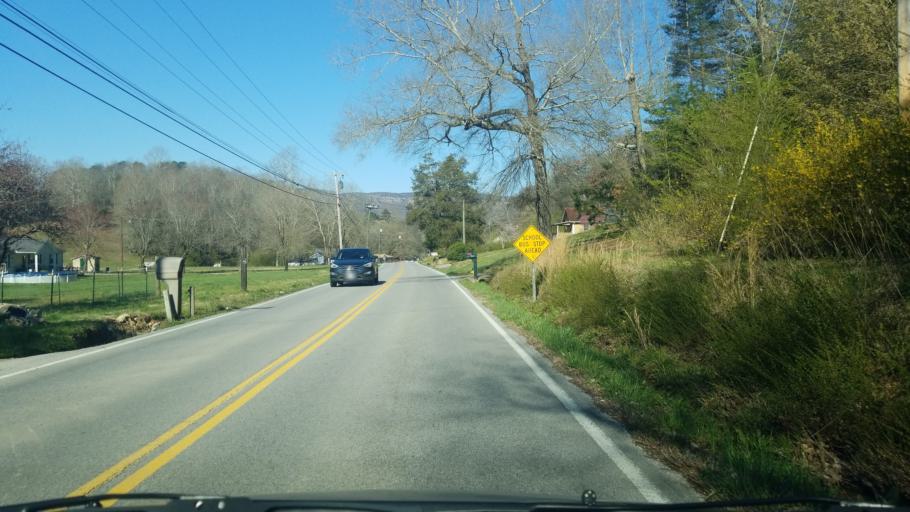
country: US
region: Tennessee
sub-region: Hamilton County
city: Soddy-Daisy
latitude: 35.2209
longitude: -85.1932
